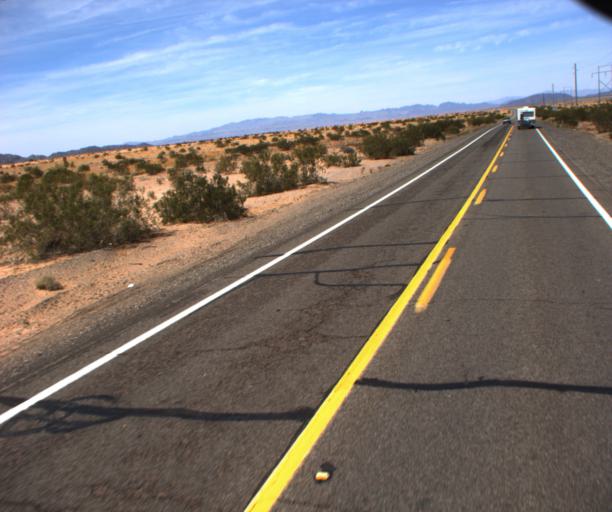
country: US
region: Arizona
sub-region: La Paz County
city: Parker
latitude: 33.9478
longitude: -114.2169
